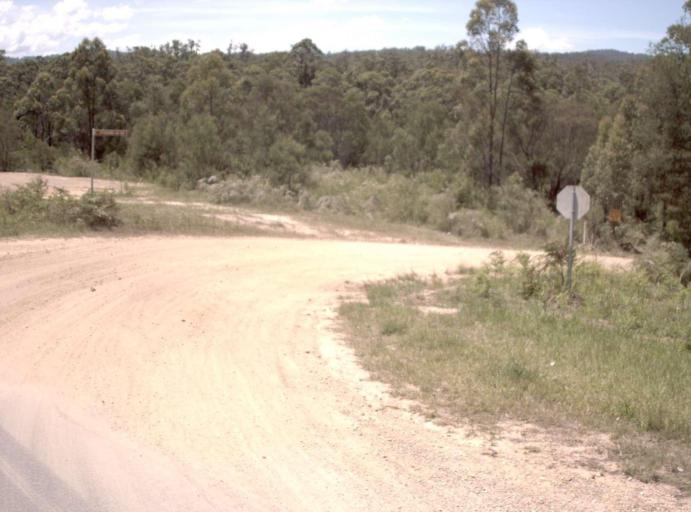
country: AU
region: New South Wales
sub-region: Bombala
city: Bombala
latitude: -37.5456
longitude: 148.9370
